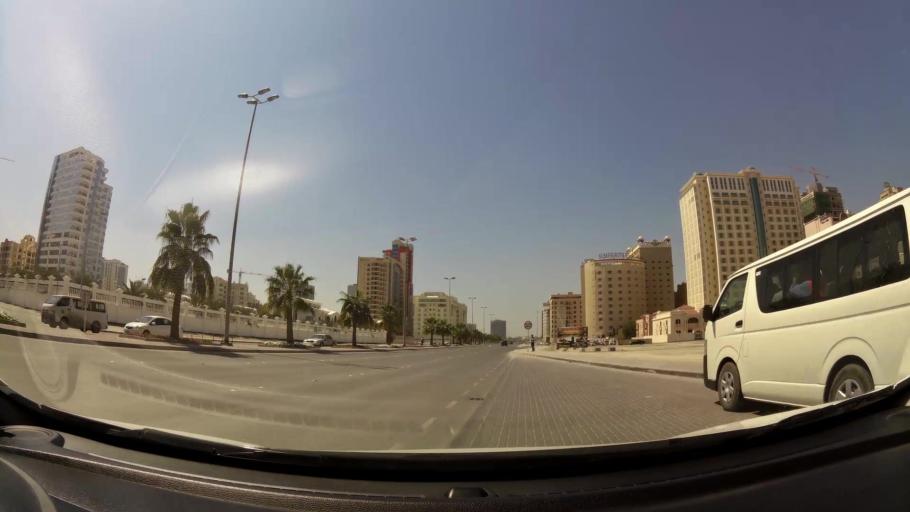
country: BH
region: Manama
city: Manama
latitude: 26.2167
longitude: 50.6073
